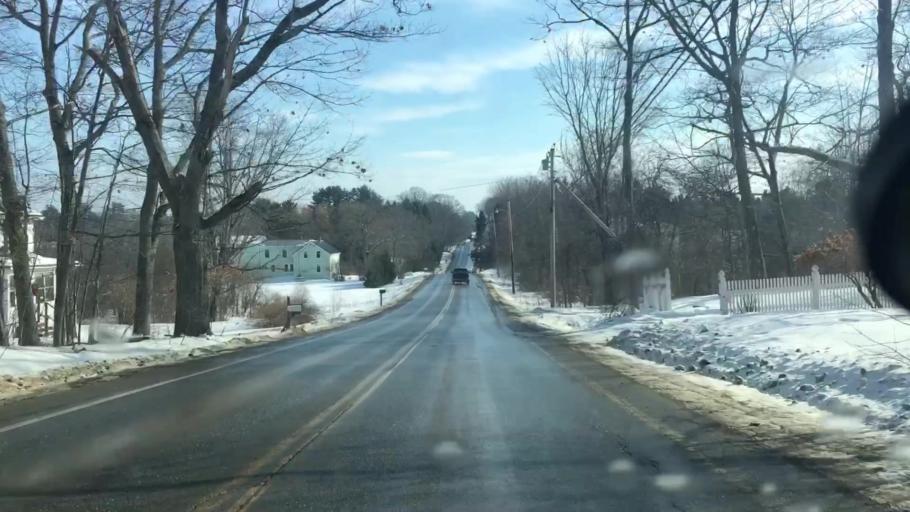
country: US
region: Maine
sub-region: Penobscot County
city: Bangor
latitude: 44.8455
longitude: -68.8364
